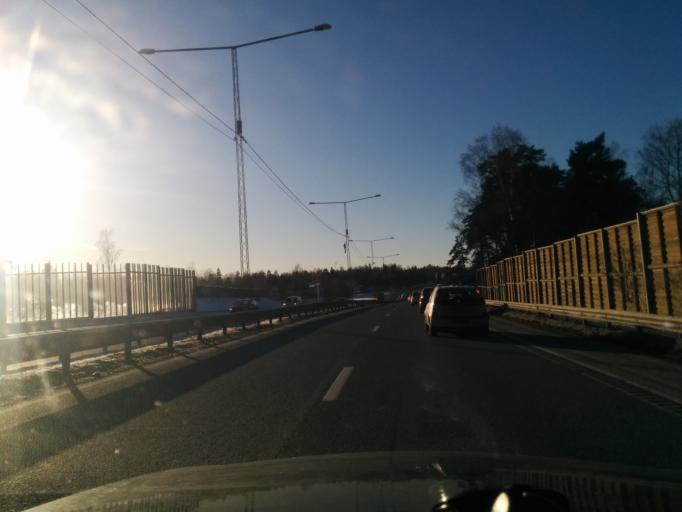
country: SE
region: Stockholm
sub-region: Taby Kommun
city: Taby
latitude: 59.4471
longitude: 18.1250
